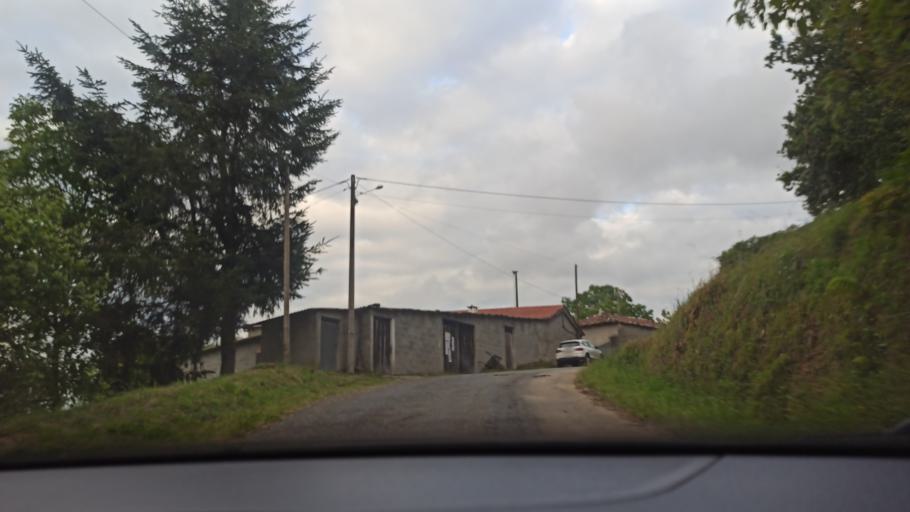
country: ES
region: Galicia
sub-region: Provincia da Coruna
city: Santiso
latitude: 42.8271
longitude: -8.1420
